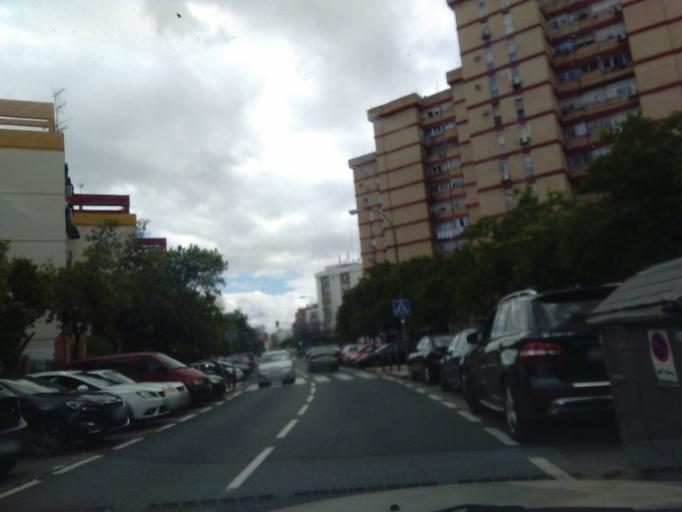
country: ES
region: Andalusia
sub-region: Provincia de Sevilla
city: Sevilla
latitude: 37.3741
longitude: -5.9531
